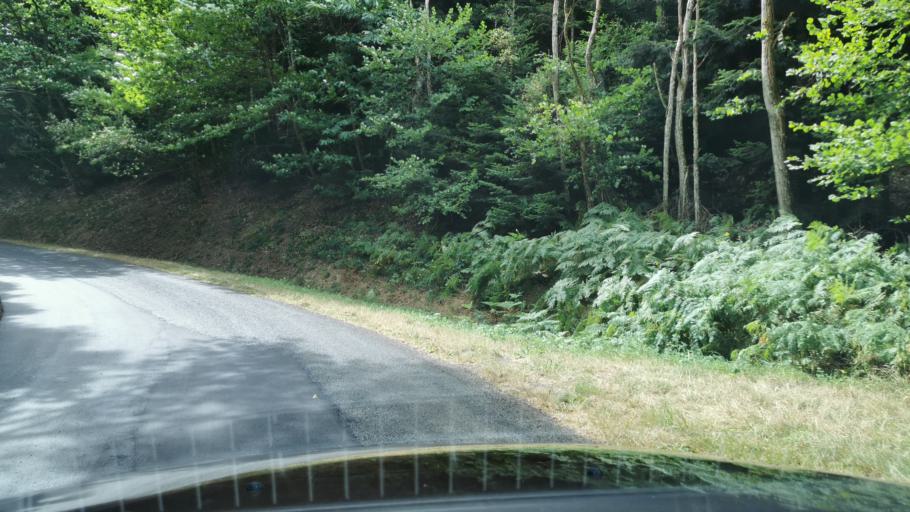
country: FR
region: Bourgogne
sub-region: Departement de Saone-et-Loire
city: Montcenis
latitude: 46.7944
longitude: 4.3705
